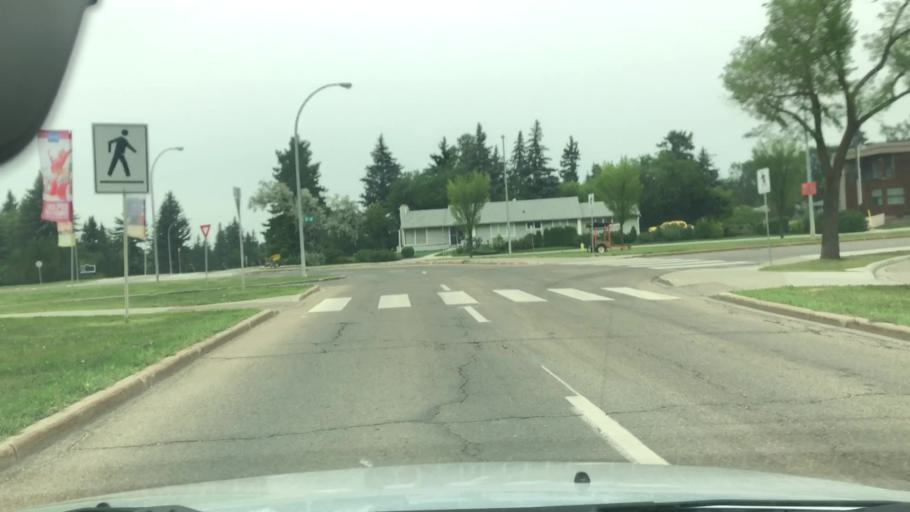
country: CA
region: Alberta
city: Edmonton
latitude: 53.5224
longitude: -113.5401
